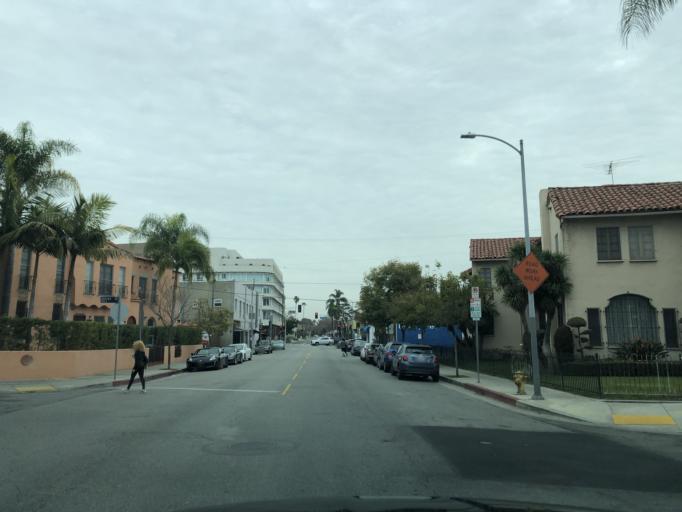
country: US
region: California
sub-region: Los Angeles County
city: West Hollywood
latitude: 34.0606
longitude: -118.3460
